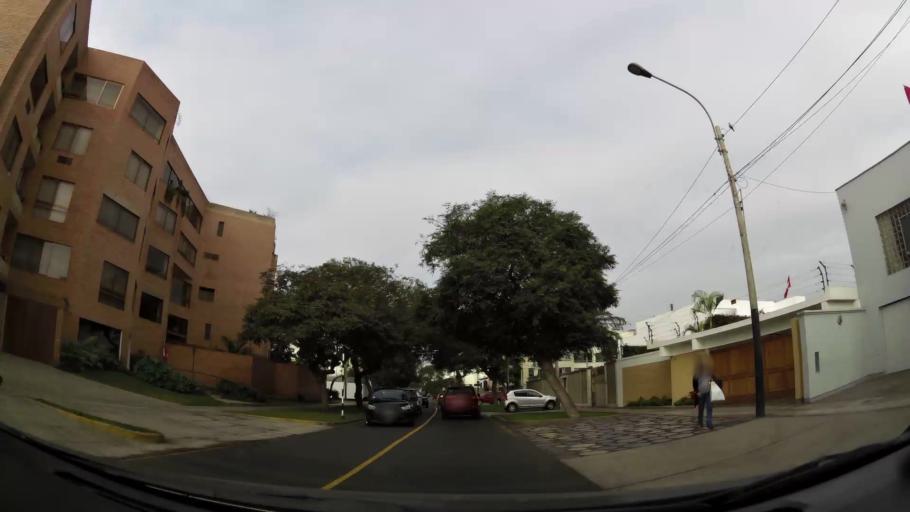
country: PE
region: Lima
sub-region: Lima
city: San Isidro
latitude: -12.0988
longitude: -77.0541
